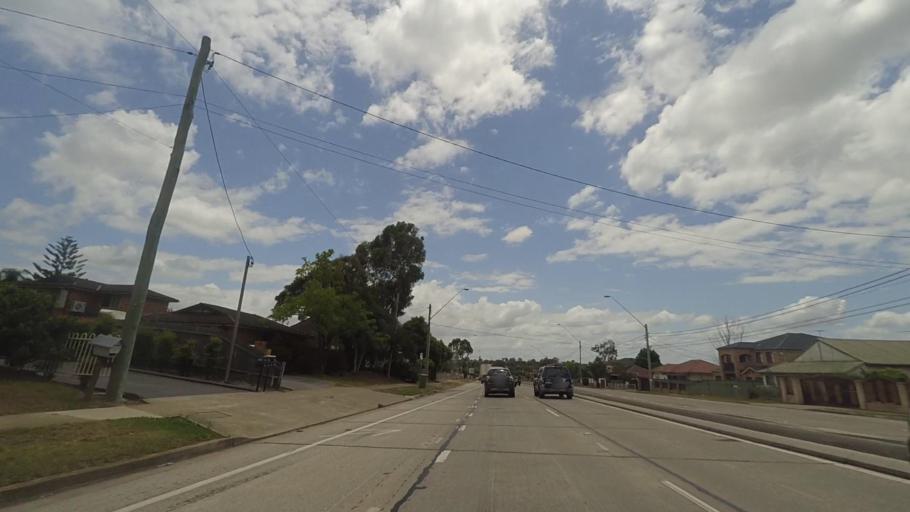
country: AU
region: New South Wales
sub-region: Fairfield
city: Cabramatta West
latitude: -33.8828
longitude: 150.9239
